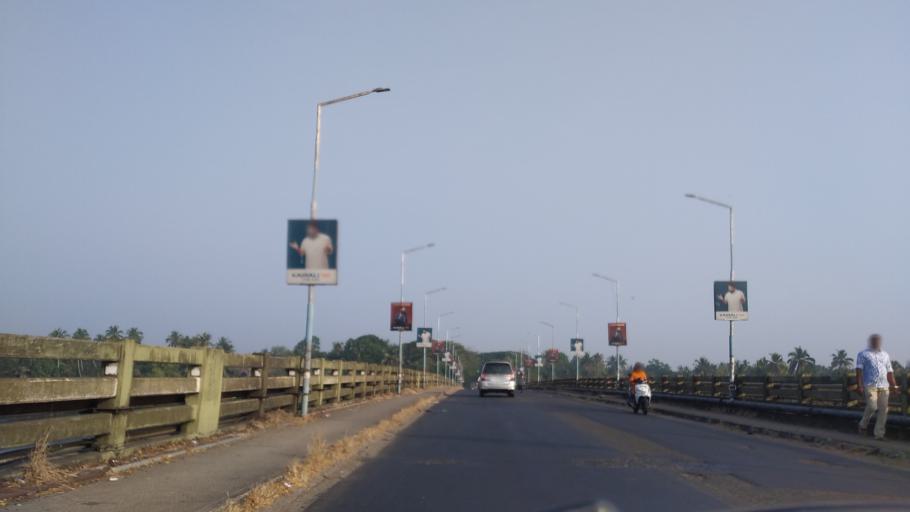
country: IN
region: Kerala
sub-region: Thrissur District
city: Kodungallur
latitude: 10.1987
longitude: 76.2007
